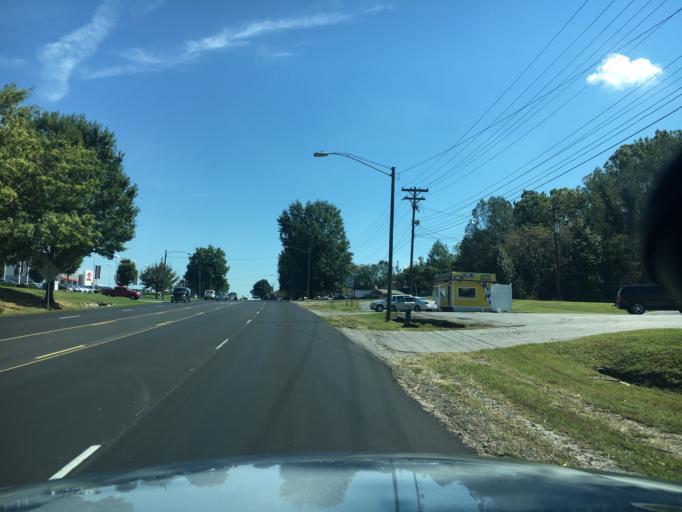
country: US
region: North Carolina
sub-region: Catawba County
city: Hickory
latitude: 35.7120
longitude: -81.3284
